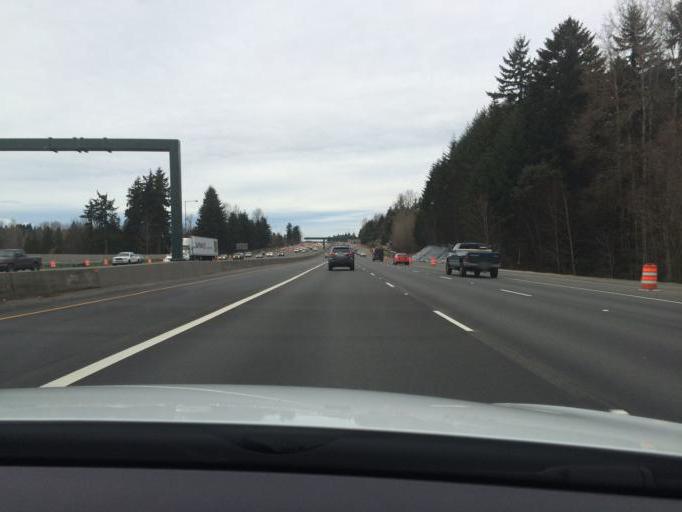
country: US
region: Washington
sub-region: King County
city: Kingsgate
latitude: 47.7324
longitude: -122.1882
